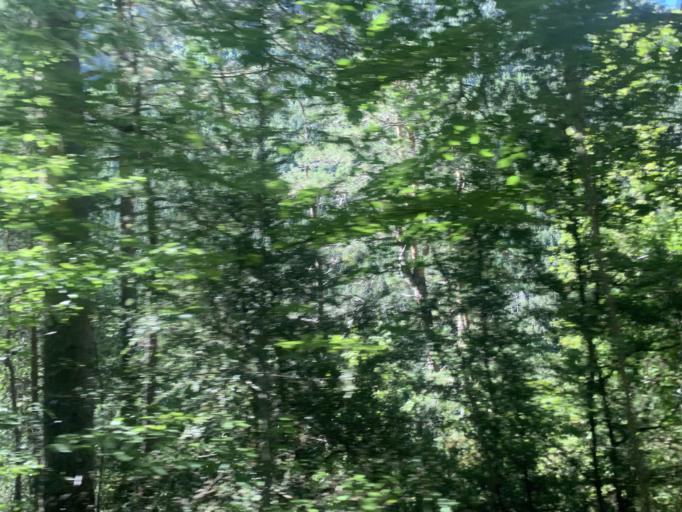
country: ES
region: Aragon
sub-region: Provincia de Huesca
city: Broto
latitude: 42.6546
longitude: -0.0903
